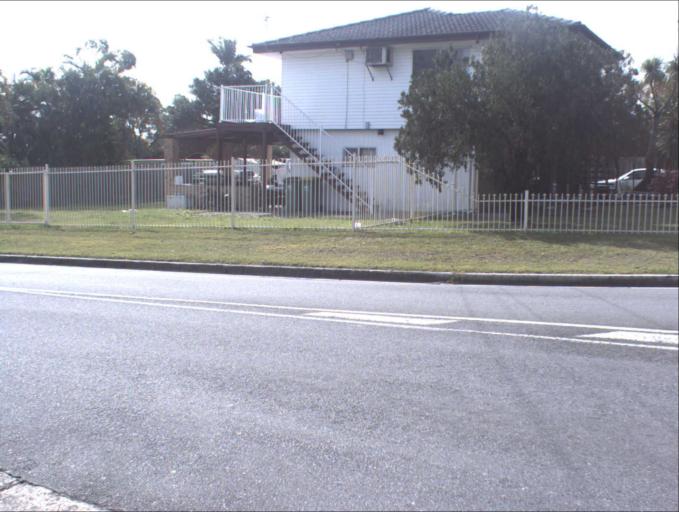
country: AU
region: Queensland
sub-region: Logan
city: Waterford West
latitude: -27.6835
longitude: 153.1199
